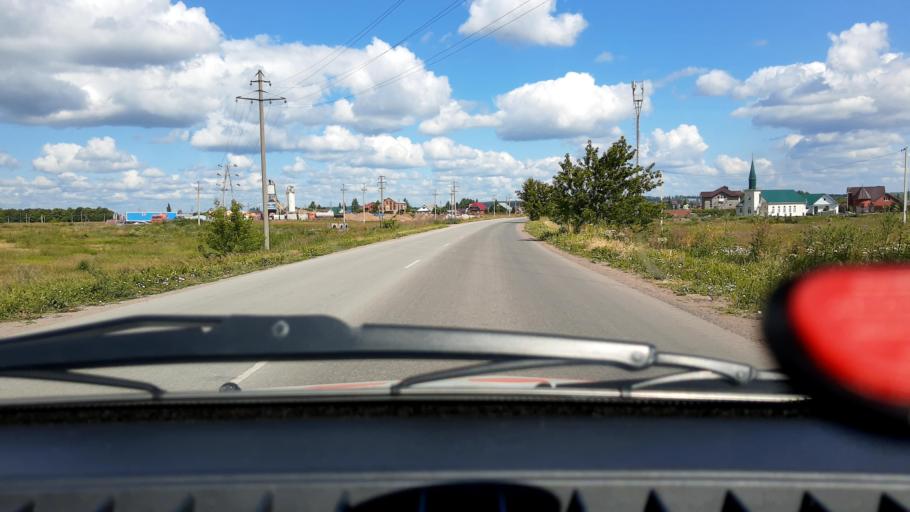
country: RU
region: Bashkortostan
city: Avdon
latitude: 54.4876
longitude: 55.8867
